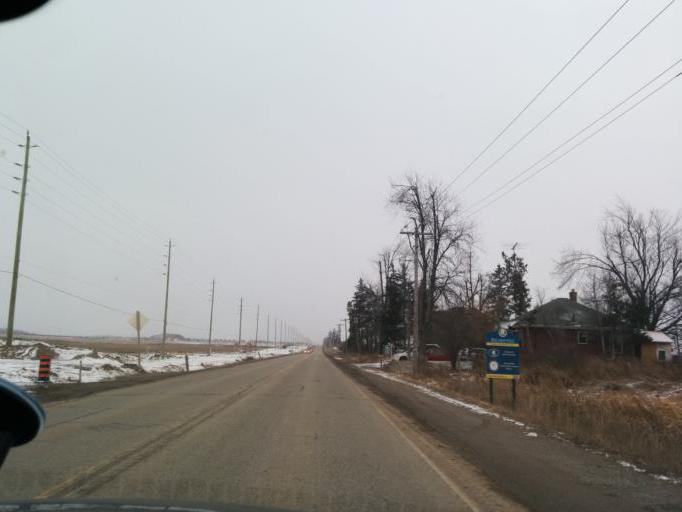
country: CA
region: Ontario
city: Brampton
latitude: 43.6935
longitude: -79.8657
